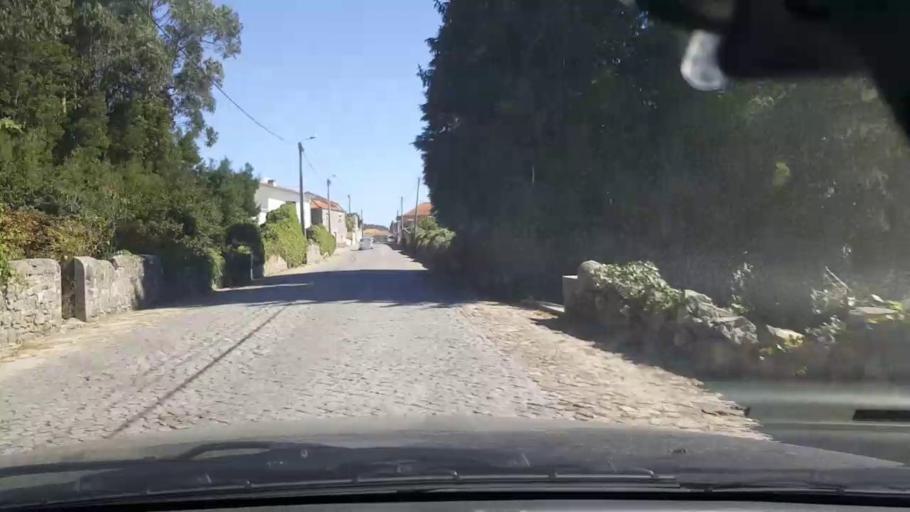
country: PT
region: Porto
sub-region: Maia
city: Gemunde
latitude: 41.3101
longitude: -8.6542
